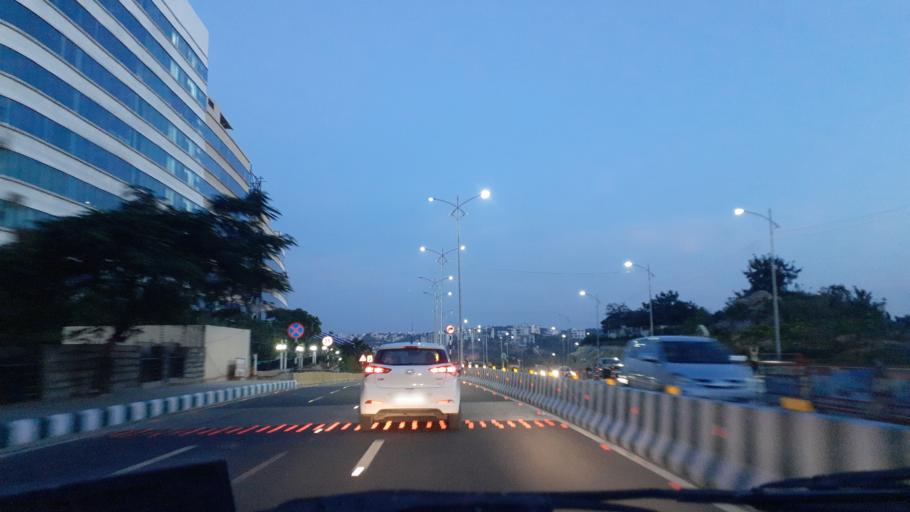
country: IN
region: Telangana
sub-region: Rangareddi
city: Kukatpalli
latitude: 17.4328
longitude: 78.3859
